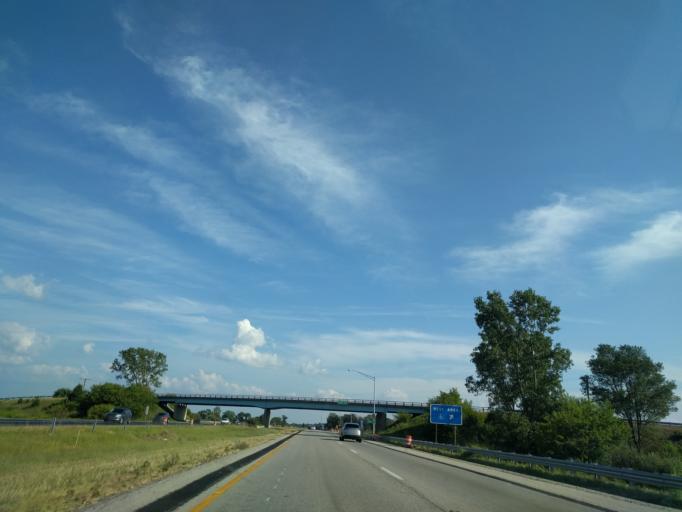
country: US
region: Indiana
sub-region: Boone County
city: Thorntown
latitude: 40.1787
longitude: -86.5567
